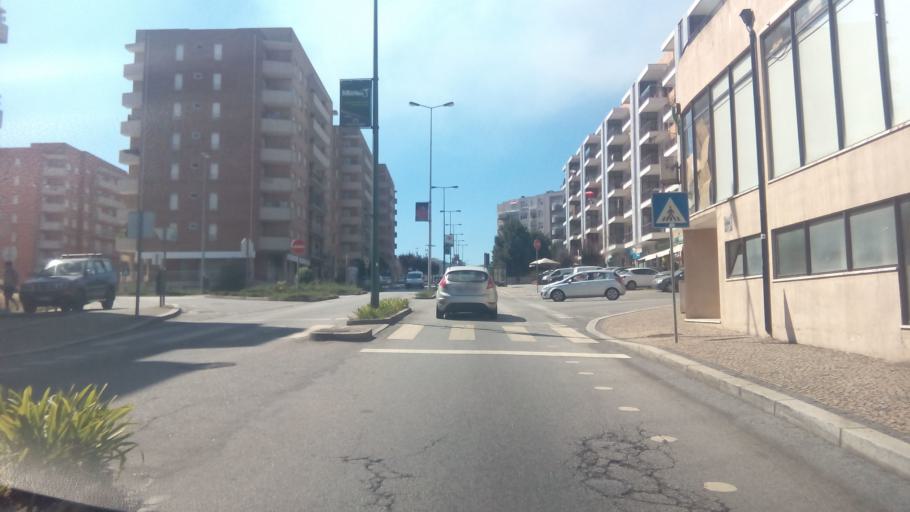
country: PT
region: Porto
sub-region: Paredes
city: Paredes
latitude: 41.2030
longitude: -8.3282
